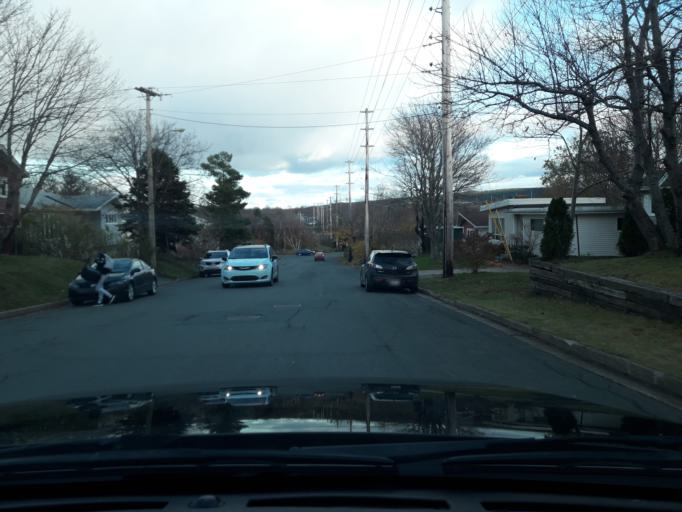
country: CA
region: Newfoundland and Labrador
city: St. John's
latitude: 47.5652
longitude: -52.7508
